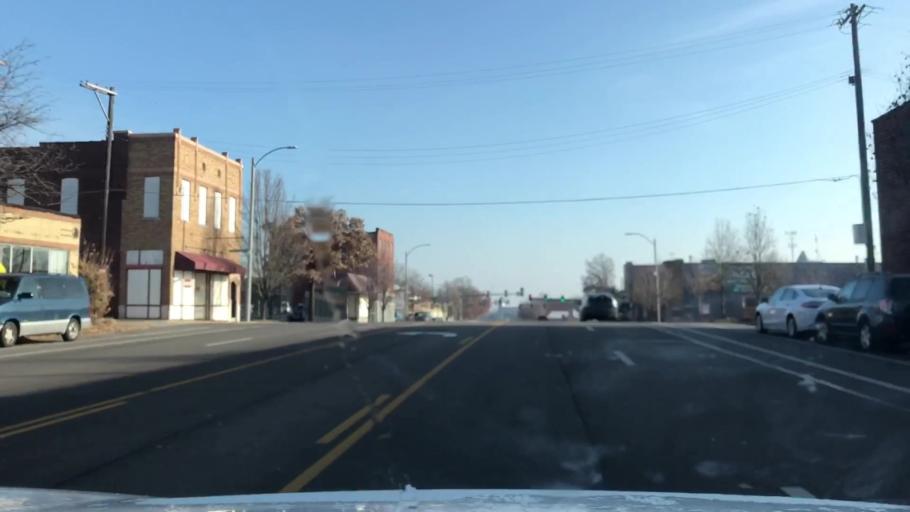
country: US
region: Missouri
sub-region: City of Saint Louis
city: St. Louis
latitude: 38.6063
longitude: -90.2197
